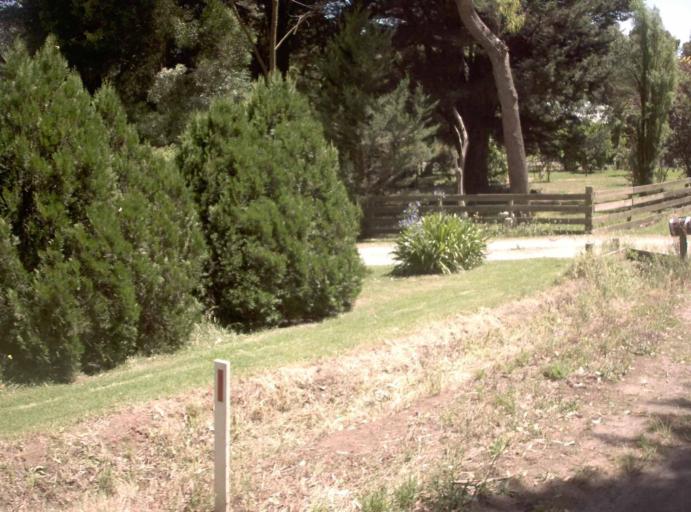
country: AU
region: Victoria
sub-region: Baw Baw
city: Warragul
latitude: -38.1803
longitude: 145.9285
